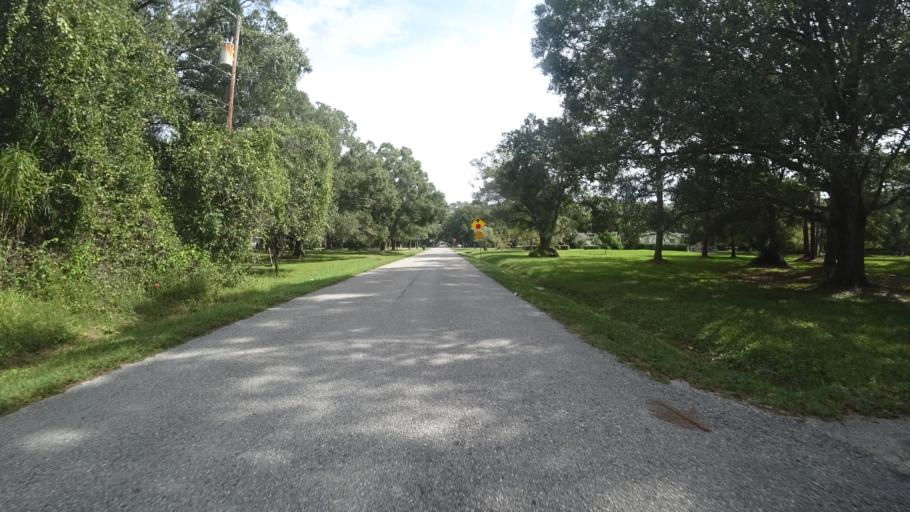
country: US
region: Florida
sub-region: Sarasota County
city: North Sarasota
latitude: 27.3870
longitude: -82.5110
